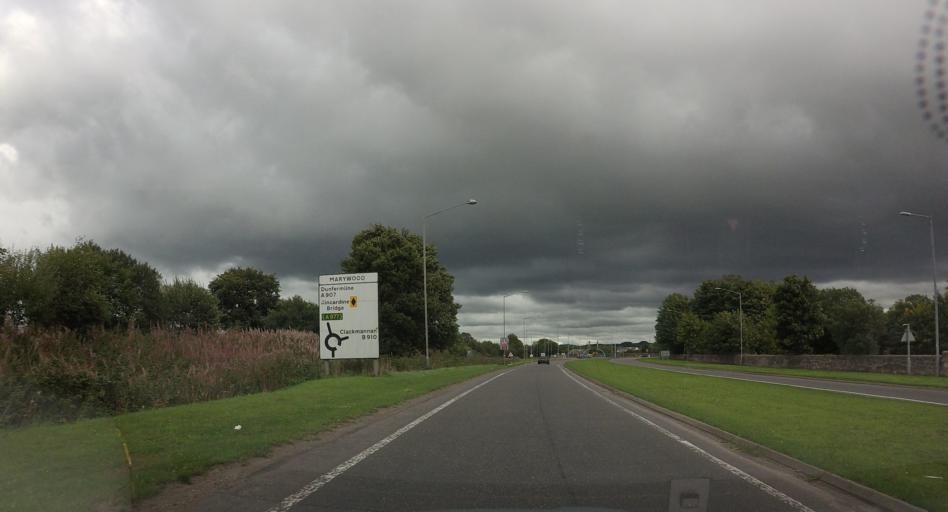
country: GB
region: Scotland
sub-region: Clackmannanshire
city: Clackmannan
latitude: 56.1146
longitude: -3.7610
